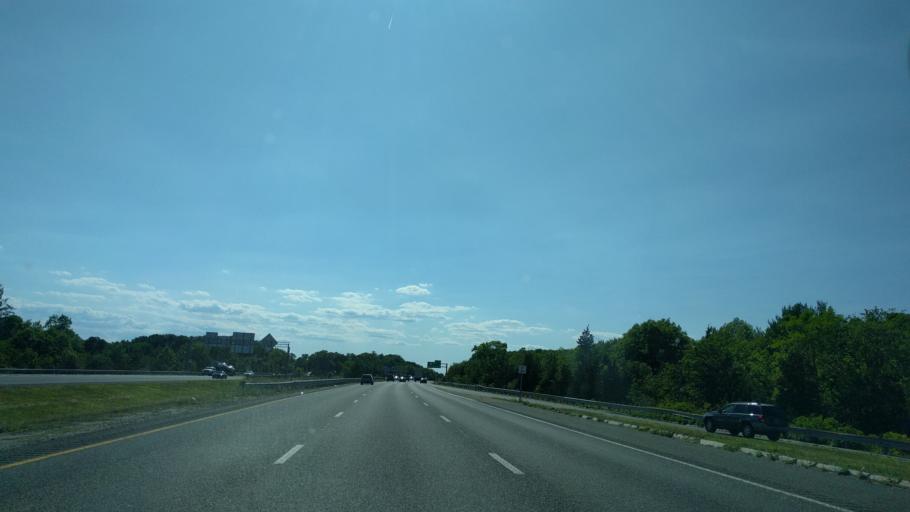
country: US
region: Massachusetts
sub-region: Norfolk County
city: Plainville
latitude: 41.9495
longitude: -71.3432
